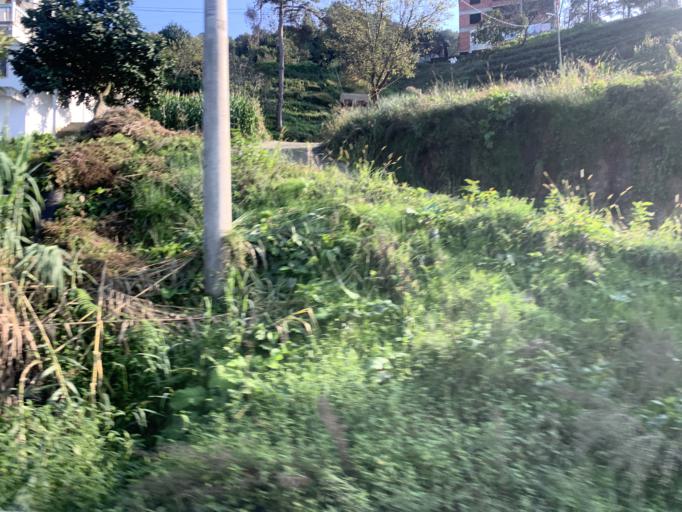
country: TR
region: Trabzon
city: Of
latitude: 40.9315
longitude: 40.2381
